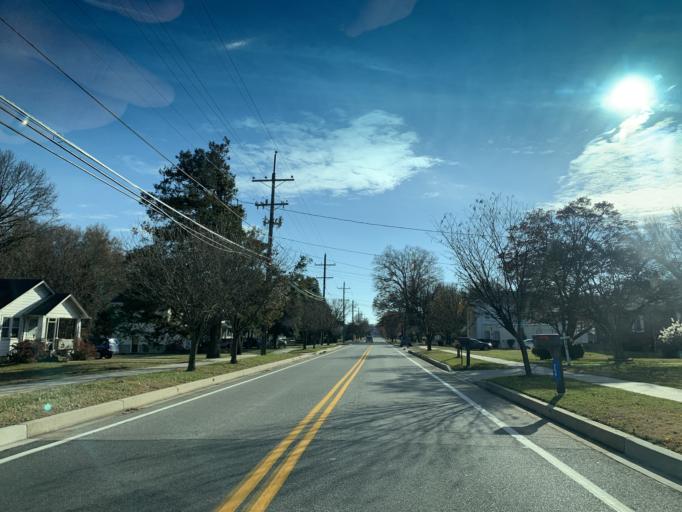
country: US
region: Maryland
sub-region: Cecil County
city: Perryville
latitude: 39.5677
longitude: -76.0706
